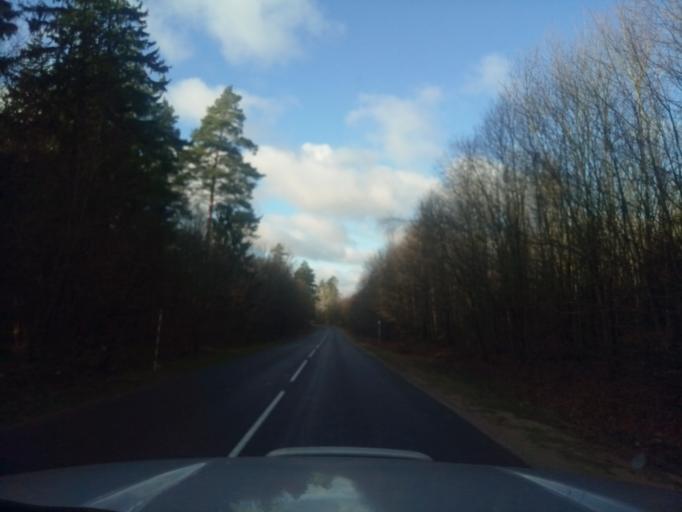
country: BY
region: Minsk
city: Kapyl'
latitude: 53.1754
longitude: 27.0115
